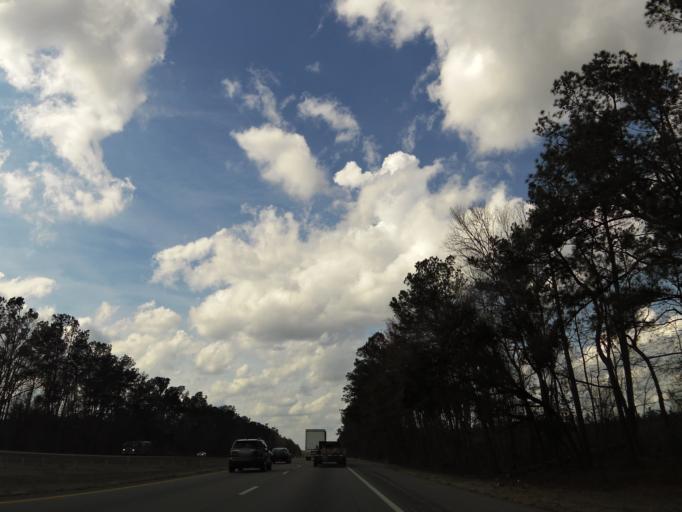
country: US
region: South Carolina
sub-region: Dorchester County
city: Ridgeville
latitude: 33.1153
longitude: -80.2668
